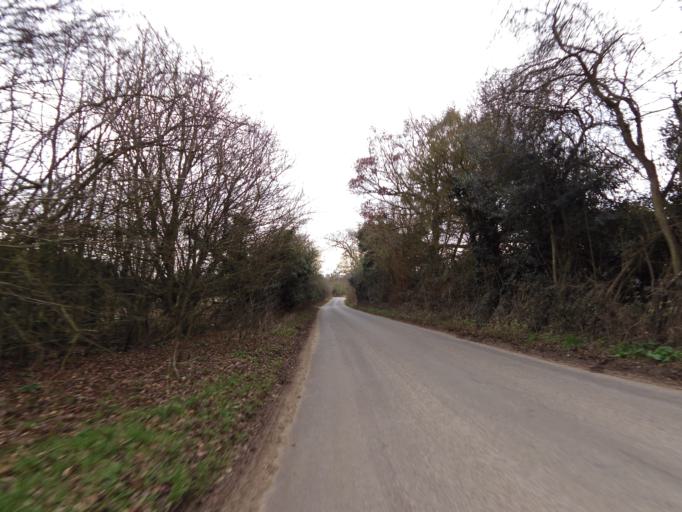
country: GB
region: England
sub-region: Suffolk
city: Woodbridge
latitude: 52.0335
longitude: 1.3080
